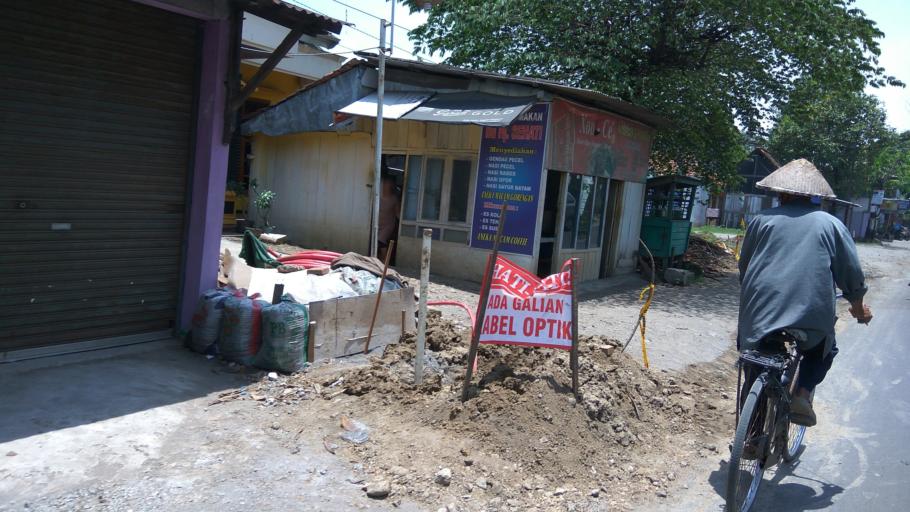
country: ID
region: Central Java
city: Mranggen
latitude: -7.0291
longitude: 110.5313
